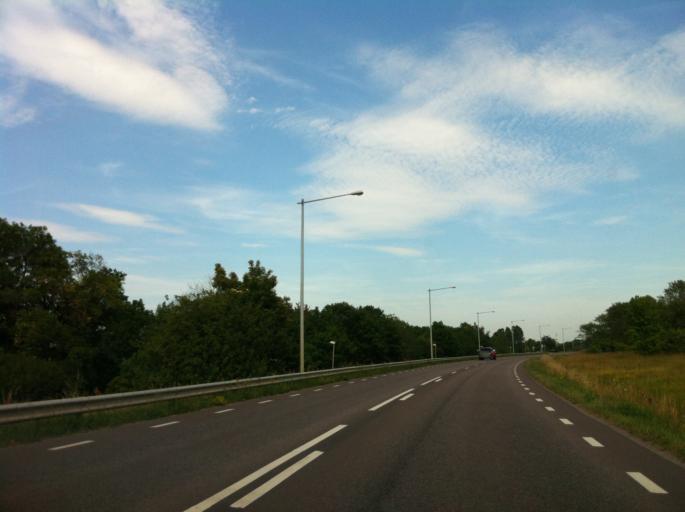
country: SE
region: Kalmar
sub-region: Borgholms Kommun
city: Borgholm
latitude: 56.8792
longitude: 16.6874
